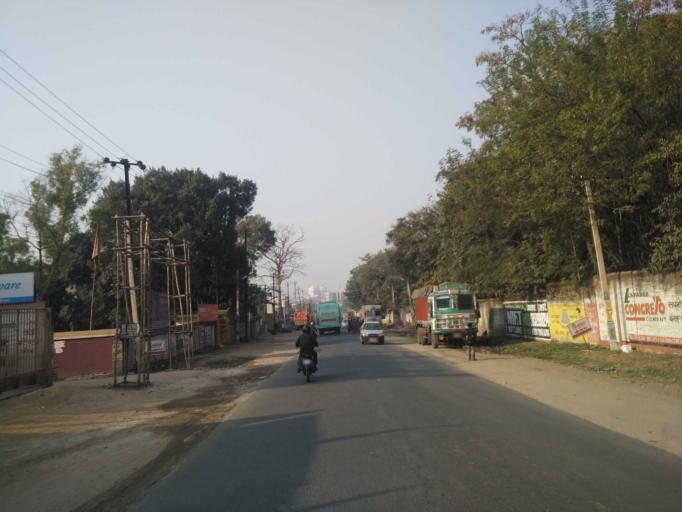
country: IN
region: Jharkhand
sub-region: Ranchi
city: Ranchi
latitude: 23.3826
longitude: 85.3669
